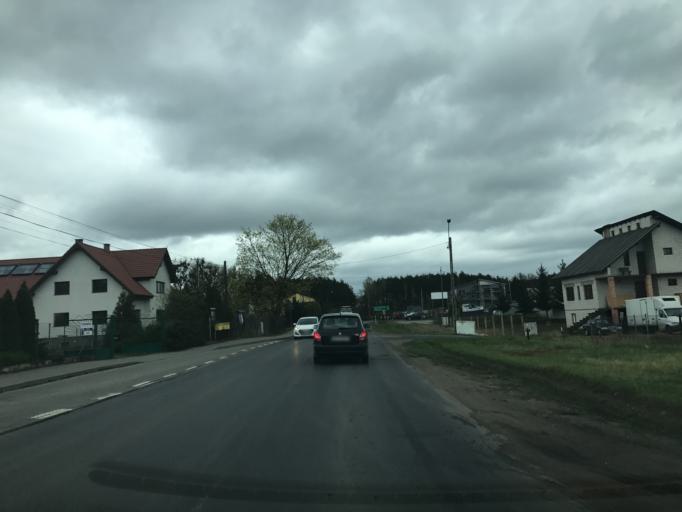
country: PL
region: Kujawsko-Pomorskie
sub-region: Bydgoszcz
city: Fordon
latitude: 53.1363
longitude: 18.1860
